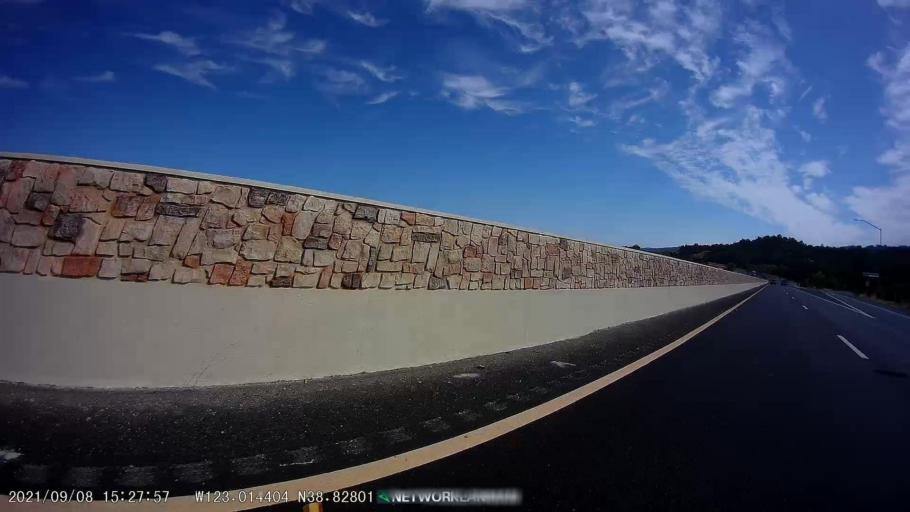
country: US
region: California
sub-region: Sonoma County
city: Cloverdale
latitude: 38.8270
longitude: -123.0143
